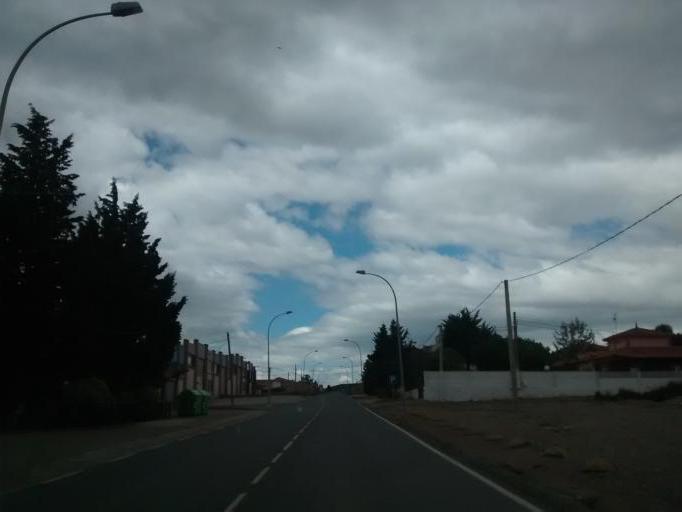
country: ES
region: La Rioja
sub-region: Provincia de La Rioja
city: Pradejon
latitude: 42.3362
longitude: -2.0743
